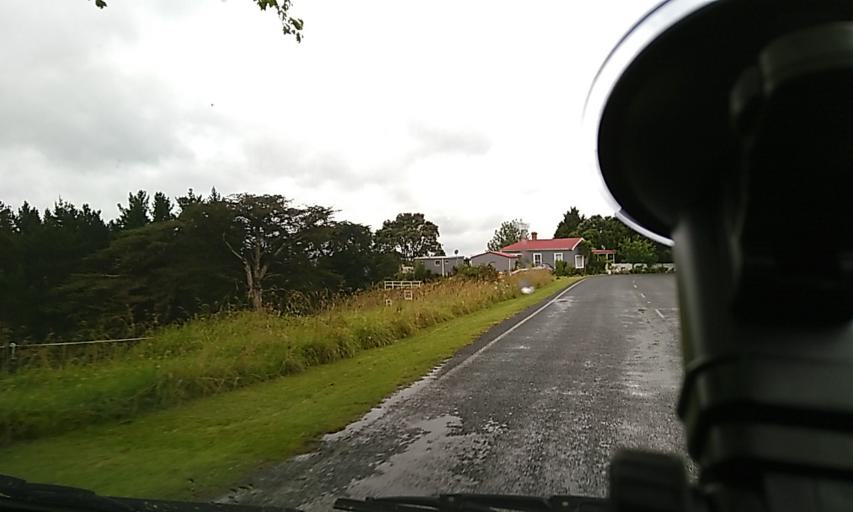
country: NZ
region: Auckland
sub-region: Auckland
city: Pukekohe East
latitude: -37.3268
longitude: 174.9157
